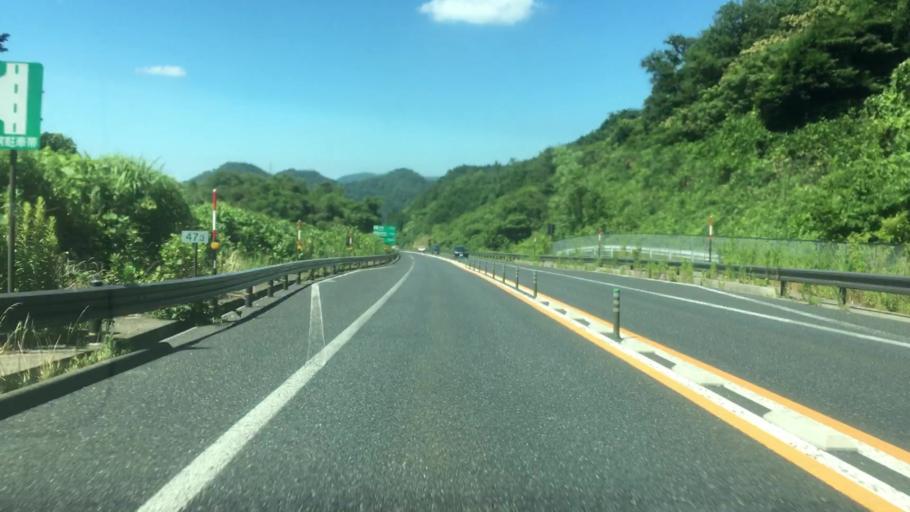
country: JP
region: Tottori
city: Tottori
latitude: 35.3644
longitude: 134.2017
